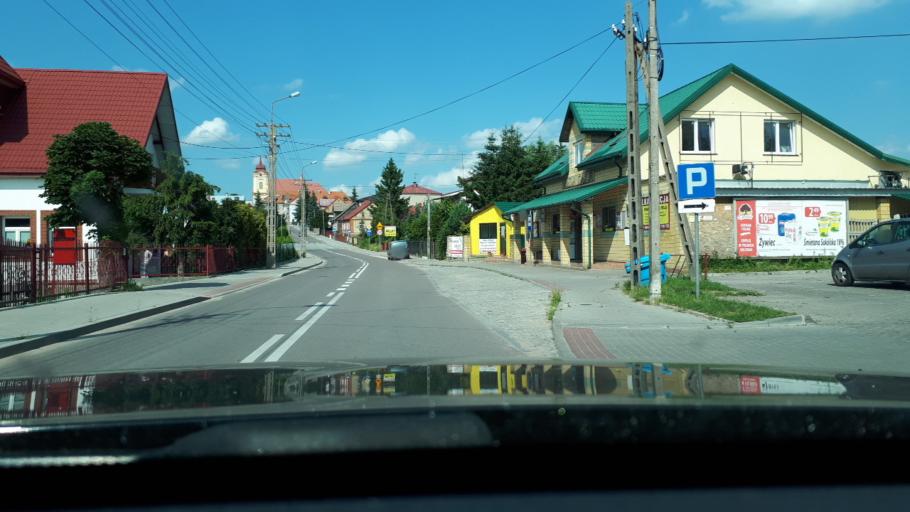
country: PL
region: Podlasie
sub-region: Powiat bialostocki
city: Choroszcz
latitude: 53.1395
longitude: 22.9849
